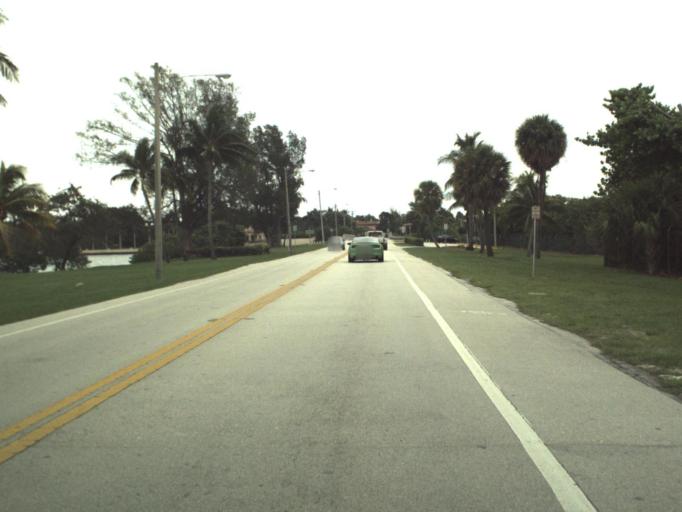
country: US
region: Florida
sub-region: Palm Beach County
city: Palm Beach
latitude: 26.6754
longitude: -80.0432
